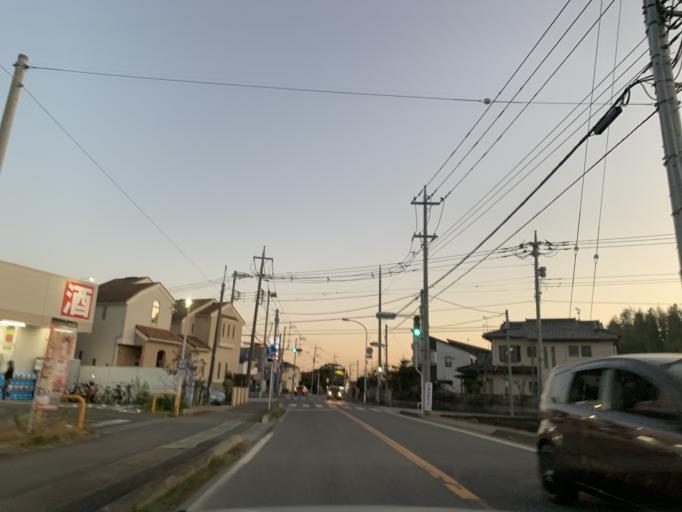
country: JP
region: Chiba
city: Nagareyama
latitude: 35.9018
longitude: 139.9020
